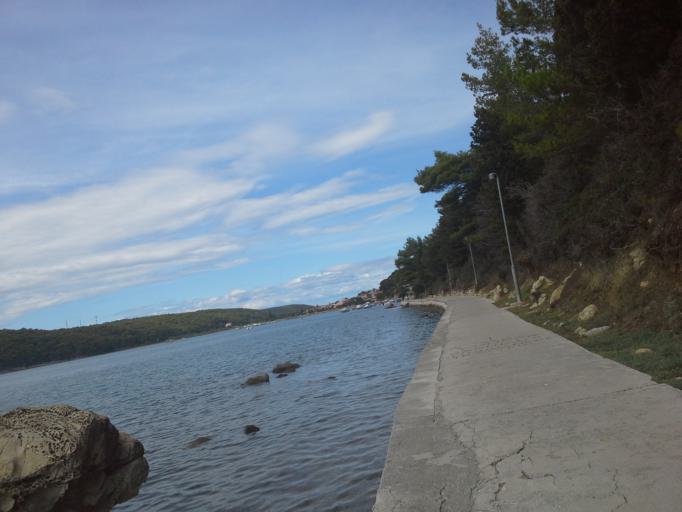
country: HR
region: Primorsko-Goranska
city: Kampor
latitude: 44.7648
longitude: 14.7455
